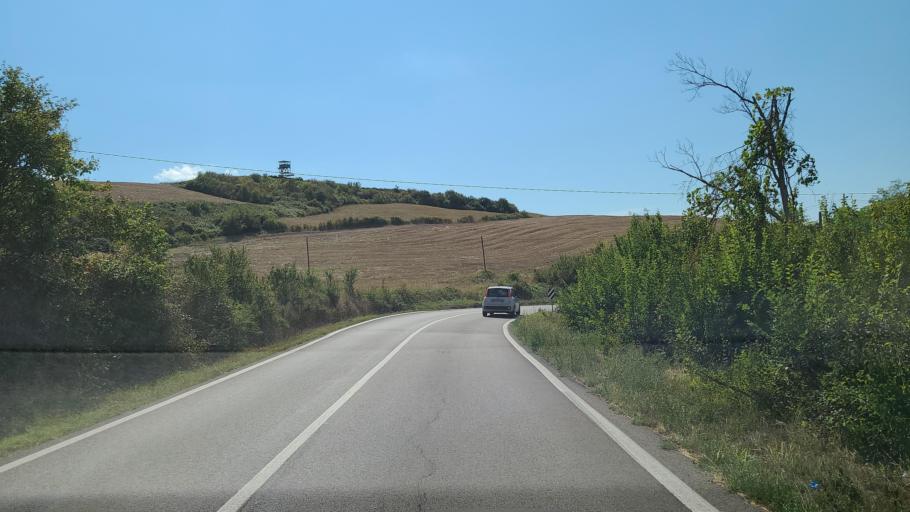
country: IT
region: Tuscany
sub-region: Province of Pisa
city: Volterra
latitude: 43.3854
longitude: 10.9107
